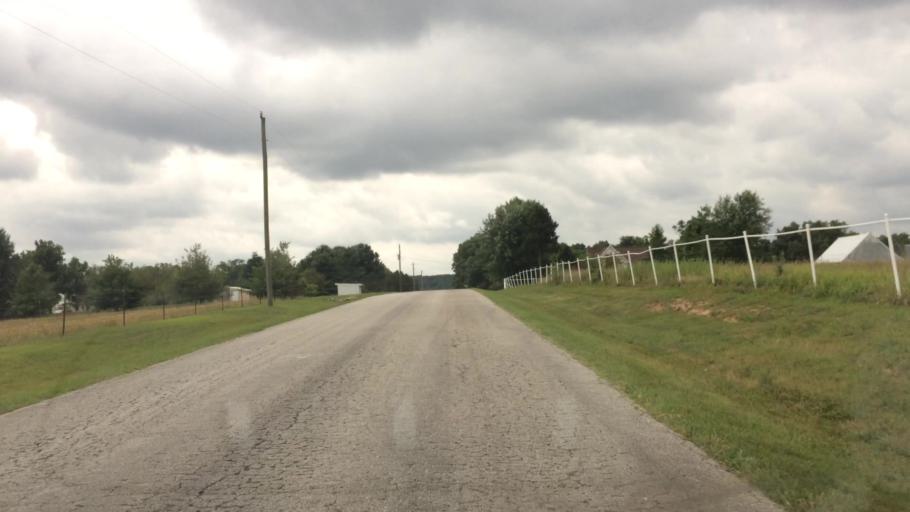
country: US
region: Missouri
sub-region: Webster County
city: Marshfield
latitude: 37.3114
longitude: -92.9845
